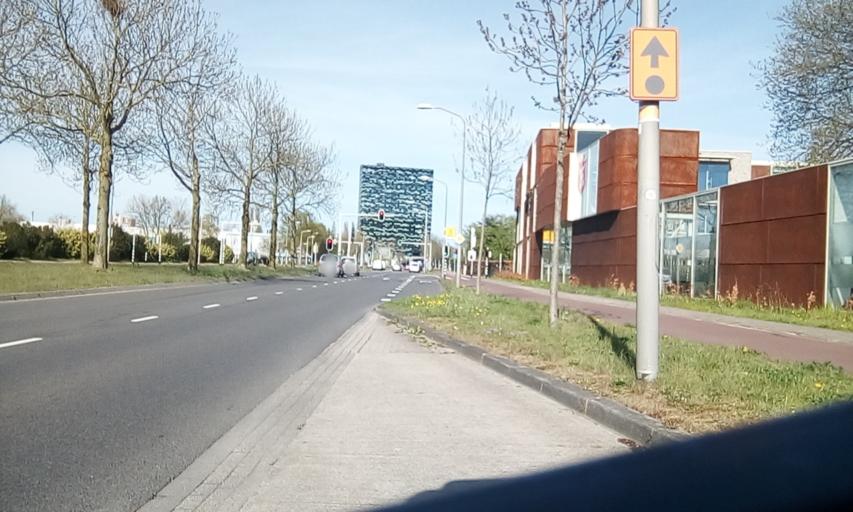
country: NL
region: Gelderland
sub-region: Gemeente Nijmegen
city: Lindenholt
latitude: 51.8206
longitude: 5.8193
